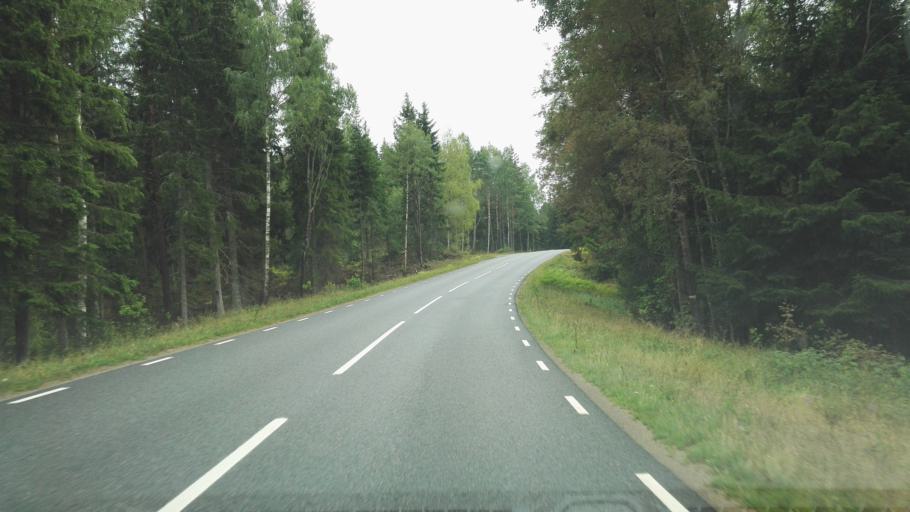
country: SE
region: Joenkoeping
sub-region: Vetlanda Kommun
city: Landsbro
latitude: 57.2841
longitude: 14.8896
